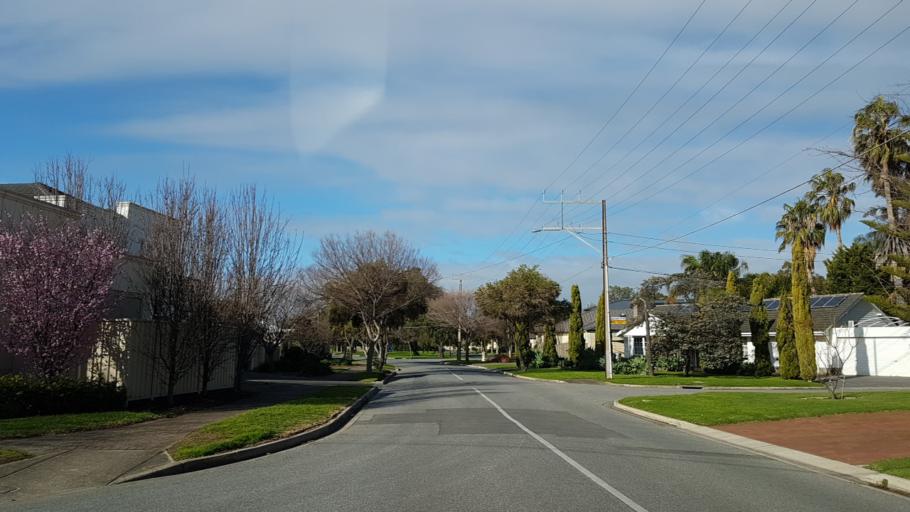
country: AU
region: South Australia
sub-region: Charles Sturt
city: Henley Beach
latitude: -34.9326
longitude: 138.5059
